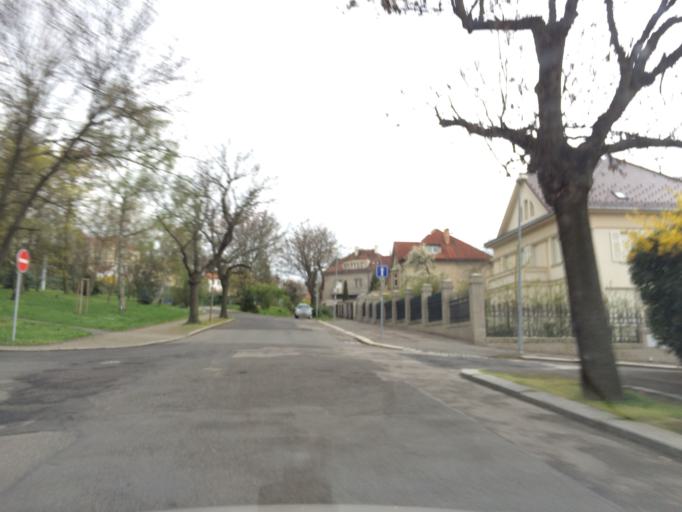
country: CZ
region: Praha
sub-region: Praha 1
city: Mala Strana
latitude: 50.0936
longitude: 14.3793
